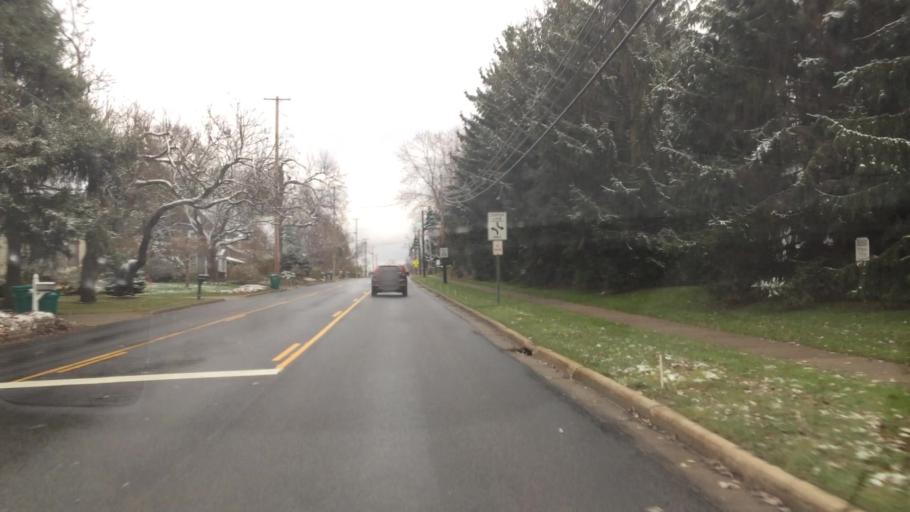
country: US
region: Ohio
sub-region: Summit County
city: Twinsburg
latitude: 41.3155
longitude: -81.4450
